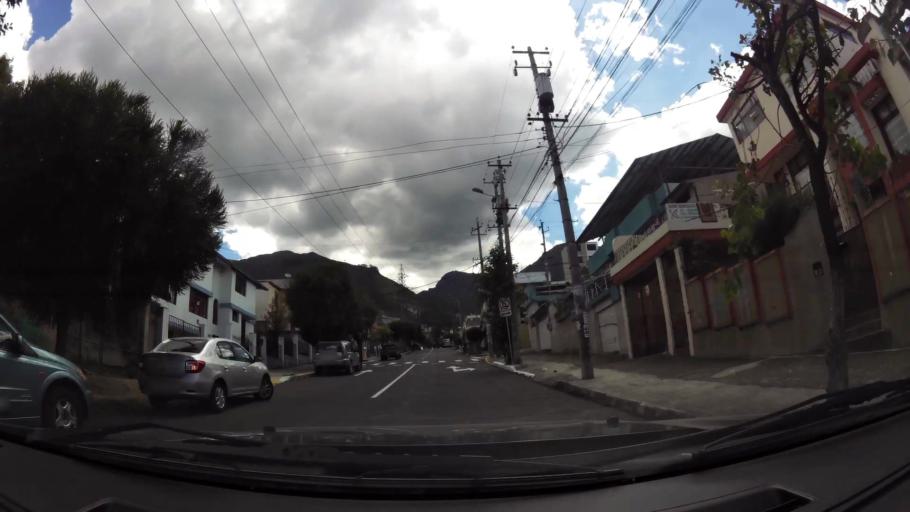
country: EC
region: Pichincha
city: Quito
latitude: -0.1874
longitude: -78.5075
